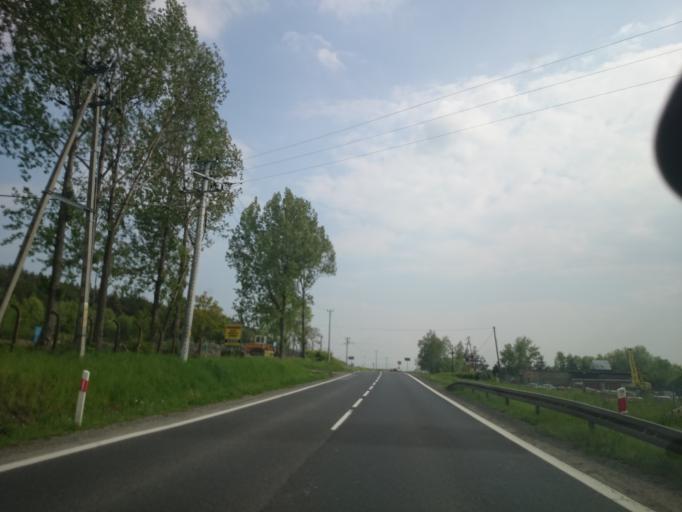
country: PL
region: Lower Silesian Voivodeship
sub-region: Powiat zabkowicki
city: Zabkowice Slaskie
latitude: 50.6413
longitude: 16.8251
